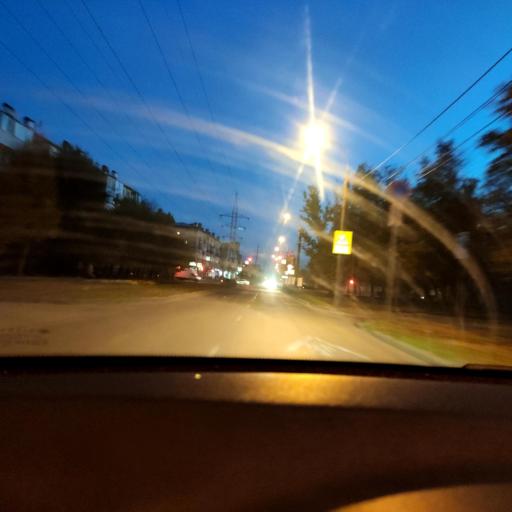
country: RU
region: Samara
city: Samara
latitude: 53.1977
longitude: 50.1713
